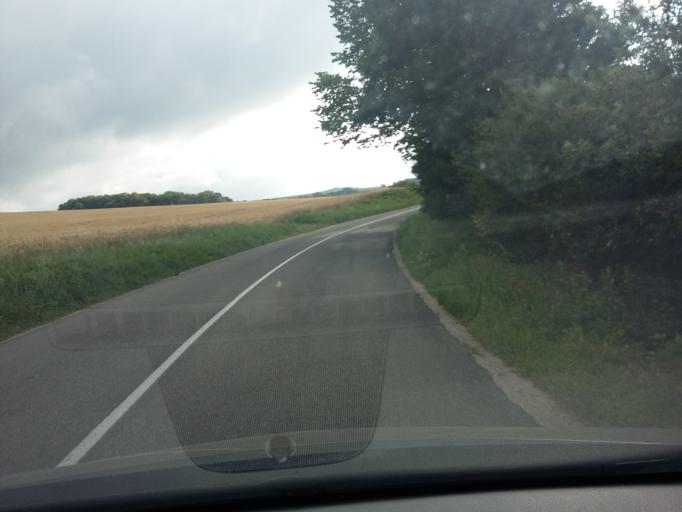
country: SK
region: Trnavsky
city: Smolenice
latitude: 48.5422
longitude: 17.3663
